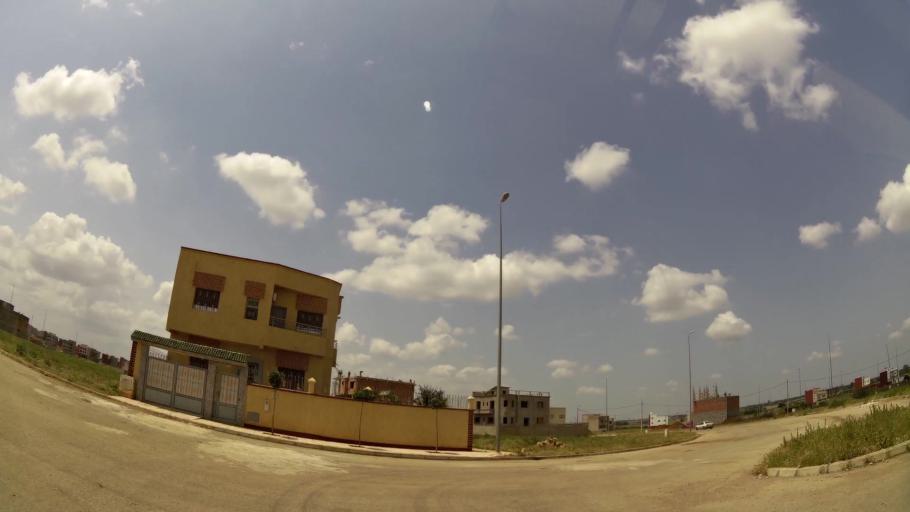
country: MA
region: Rabat-Sale-Zemmour-Zaer
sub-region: Khemisset
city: Tiflet
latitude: 34.0040
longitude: -6.5385
